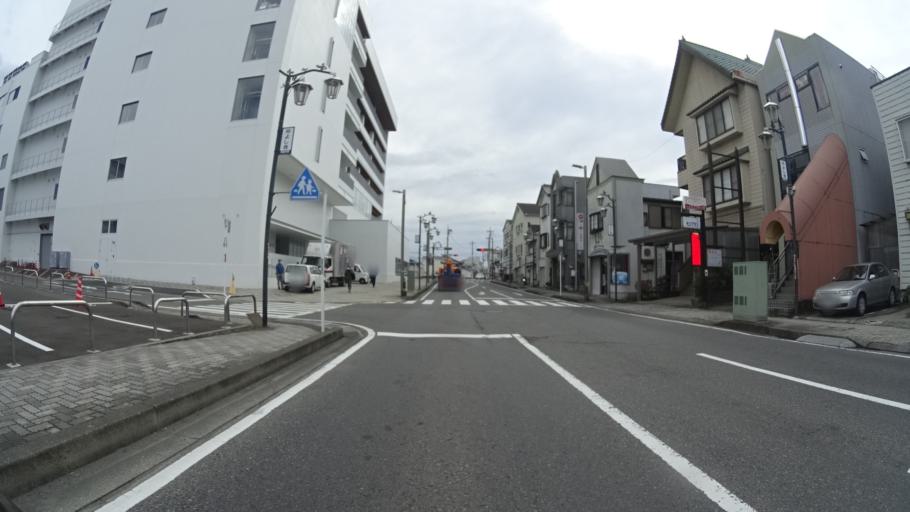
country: JP
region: Gunma
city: Numata
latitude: 36.6443
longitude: 139.0421
